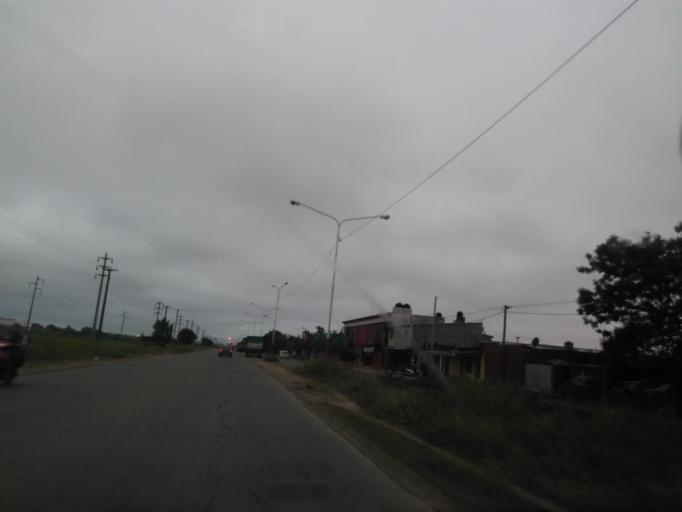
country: AR
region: Chaco
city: Resistencia
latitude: -27.4814
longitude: -58.9956
